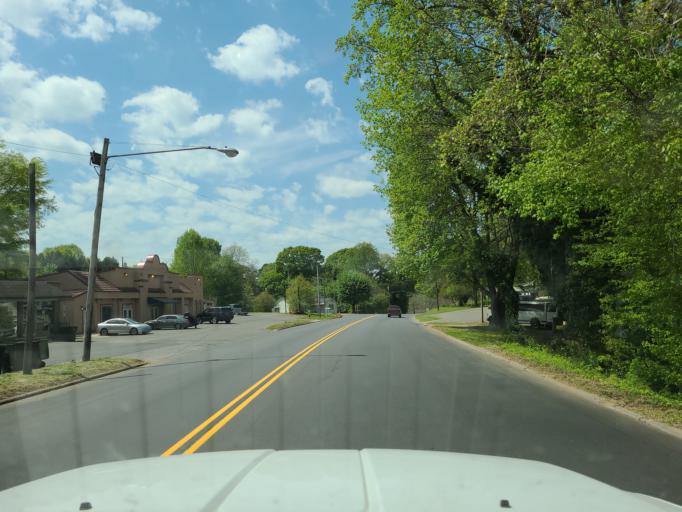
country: US
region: North Carolina
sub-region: Lincoln County
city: Lincolnton
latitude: 35.4678
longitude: -81.2640
